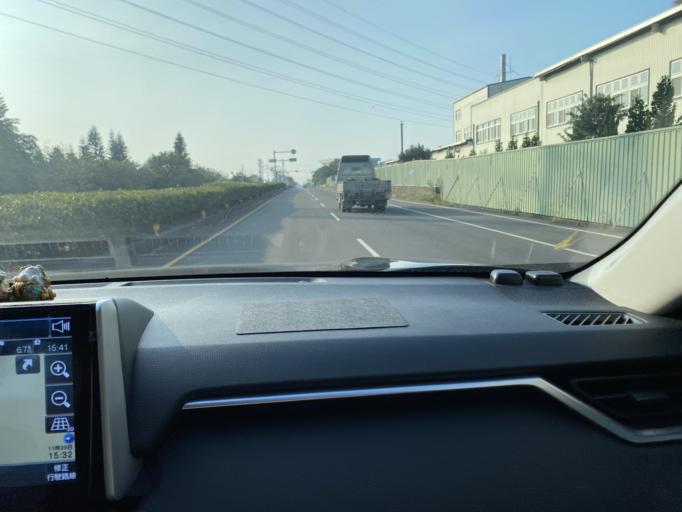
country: TW
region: Taiwan
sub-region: Changhua
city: Chang-hua
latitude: 23.9584
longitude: 120.4030
